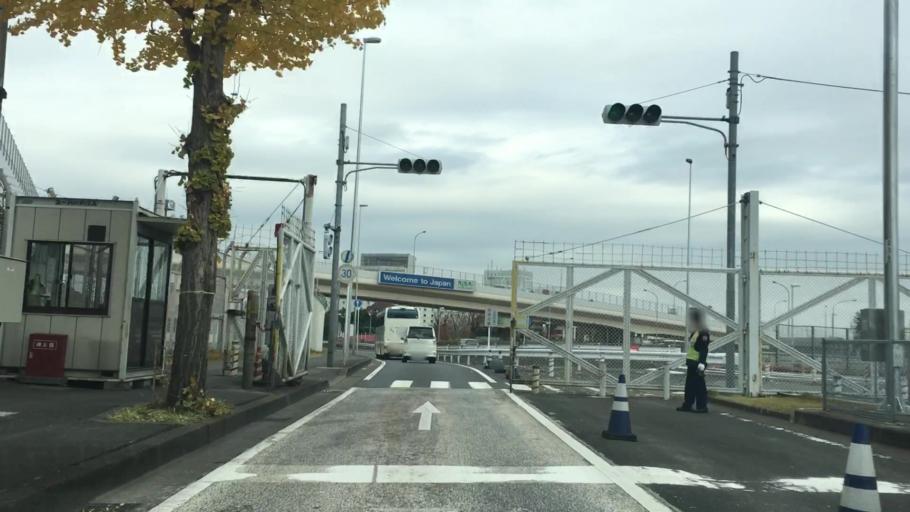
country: JP
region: Chiba
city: Narita
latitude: 35.7759
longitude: 140.3815
